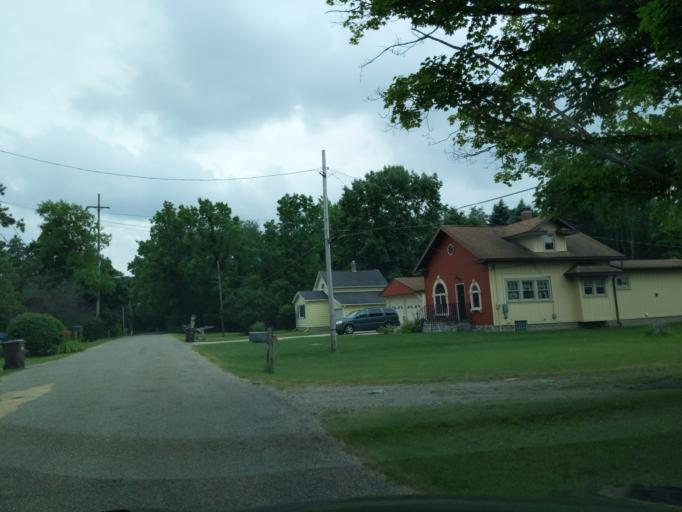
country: US
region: Michigan
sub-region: Ingham County
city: Lansing
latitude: 42.7750
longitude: -84.5587
